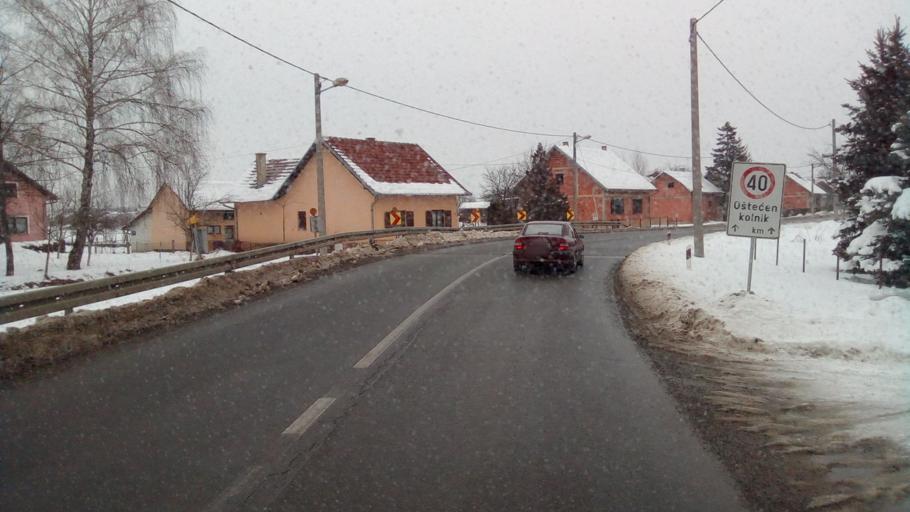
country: HR
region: Sisacko-Moslavacka
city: Petrinja
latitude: 45.4443
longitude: 16.3105
